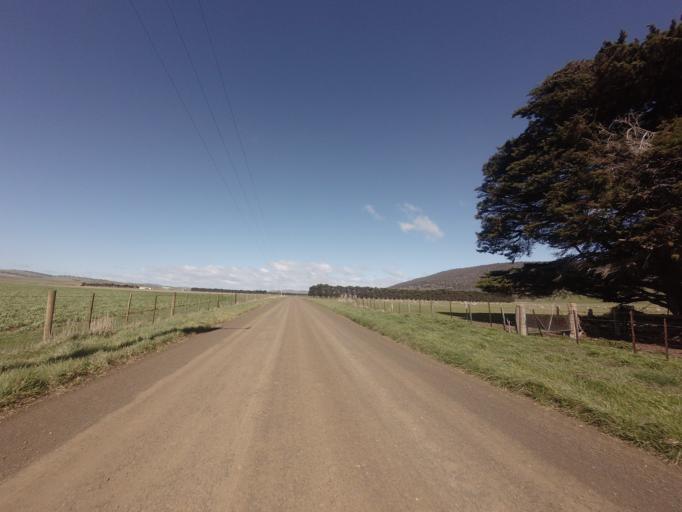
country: AU
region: Tasmania
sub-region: Northern Midlands
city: Evandale
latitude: -41.9545
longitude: 147.4360
